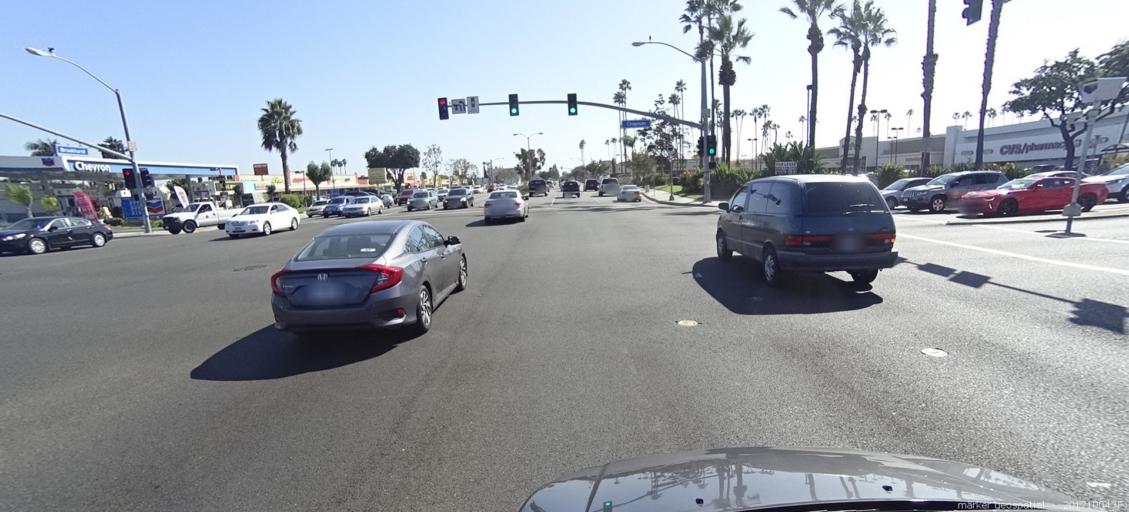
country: US
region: California
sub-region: Orange County
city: Garden Grove
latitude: 33.7888
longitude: -117.9588
